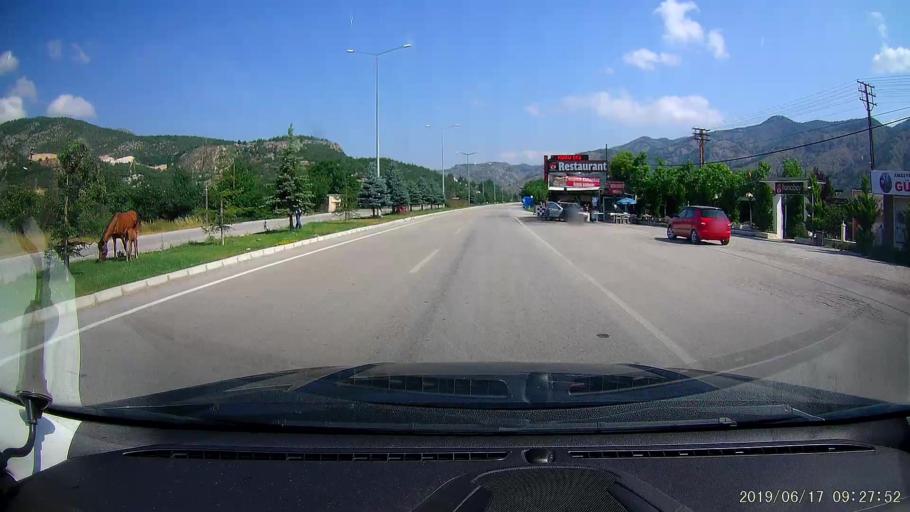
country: TR
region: Amasya
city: Amasya
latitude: 40.6818
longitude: 35.8240
